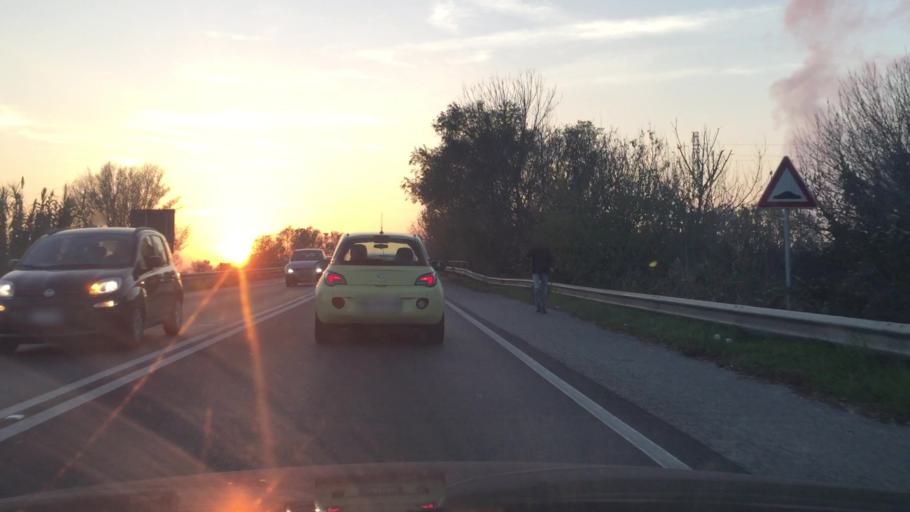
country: IT
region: Emilia-Romagna
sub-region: Provincia di Ferrara
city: Ferrara
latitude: 44.8542
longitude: 11.5991
